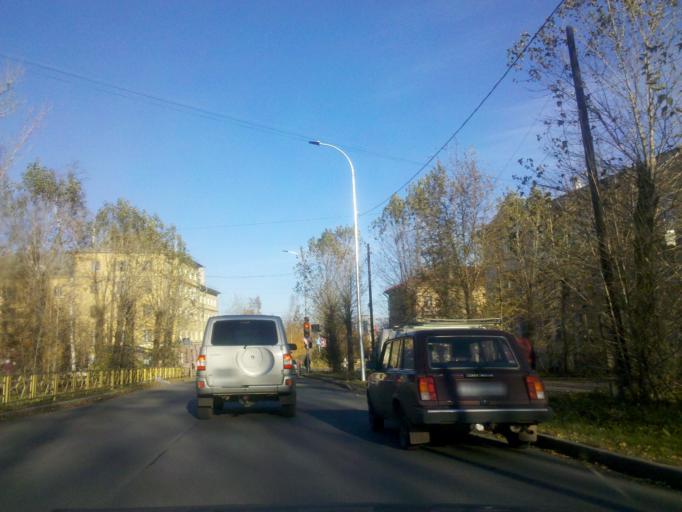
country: RU
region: Republic of Karelia
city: Petrozavodsk
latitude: 61.7980
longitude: 34.3275
